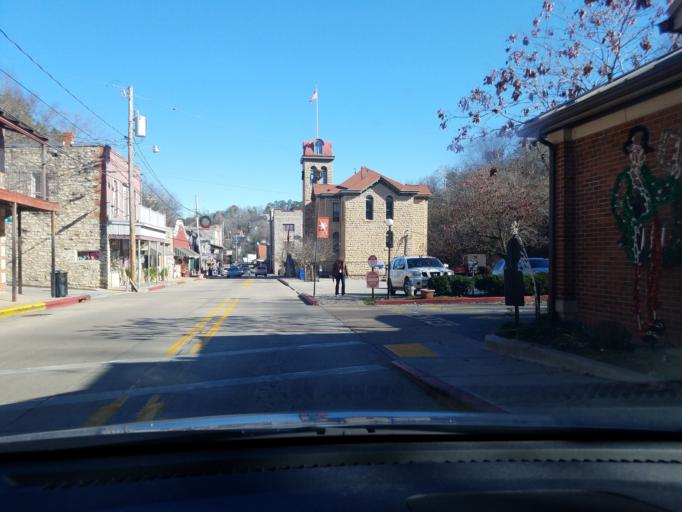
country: US
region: Arkansas
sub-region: Carroll County
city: Eureka Springs
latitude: 36.4005
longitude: -93.7396
